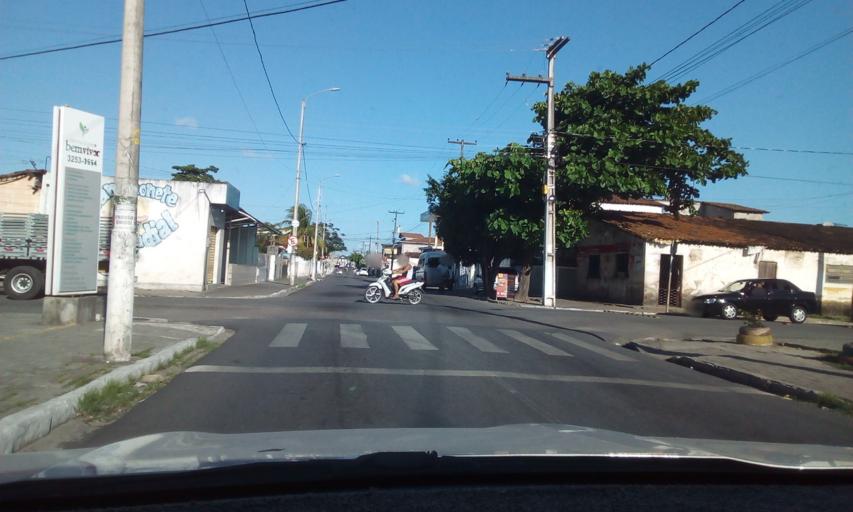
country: BR
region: Paraiba
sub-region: Bayeux
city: Bayeux
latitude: -7.1252
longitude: -34.9186
